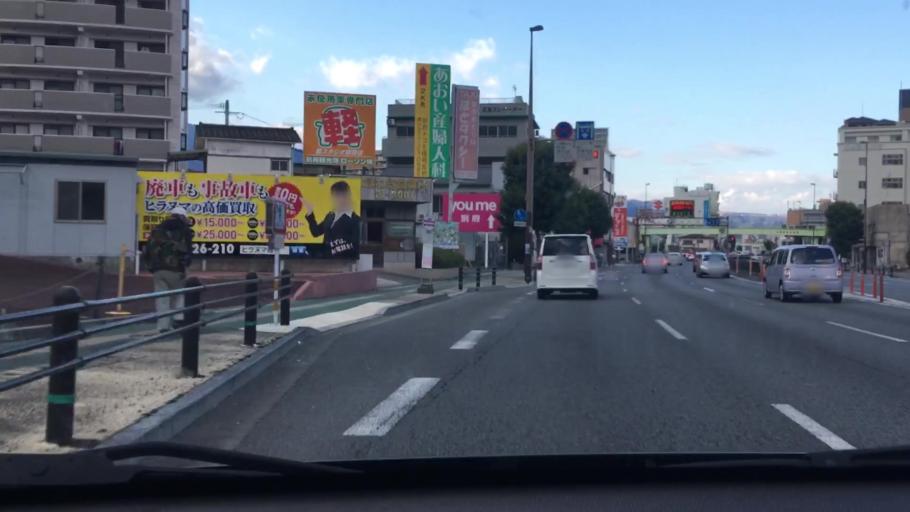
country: JP
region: Oita
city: Beppu
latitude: 33.2681
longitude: 131.5109
